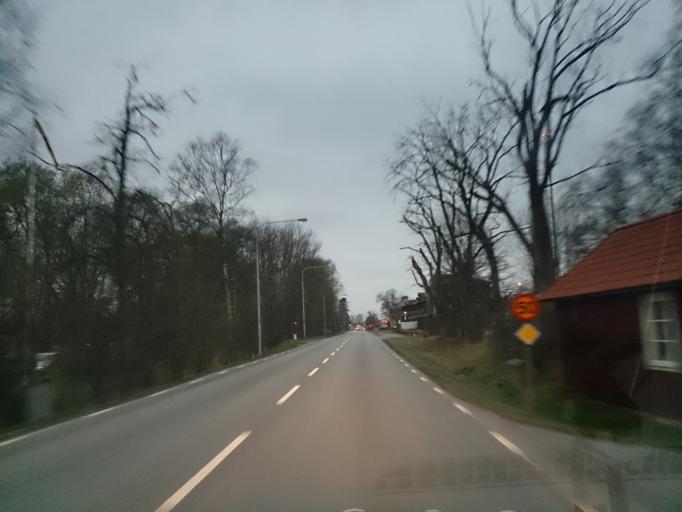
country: SE
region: OEstergoetland
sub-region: Linkopings Kommun
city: Linghem
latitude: 58.4367
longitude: 15.7918
